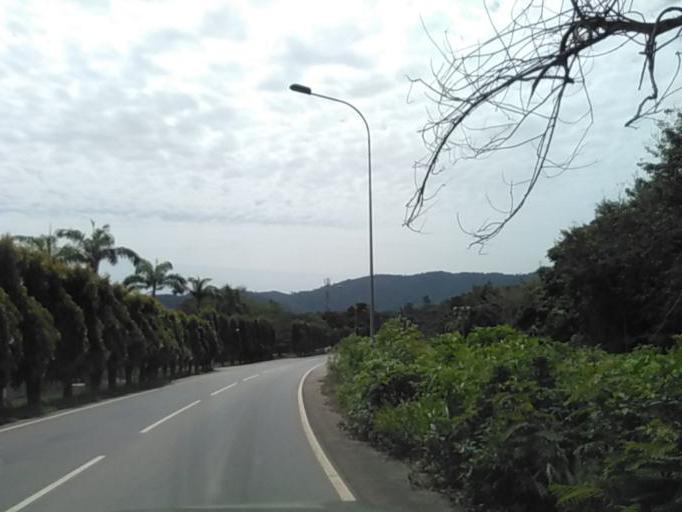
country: GH
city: Akropong
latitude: 6.2666
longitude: 0.0660
